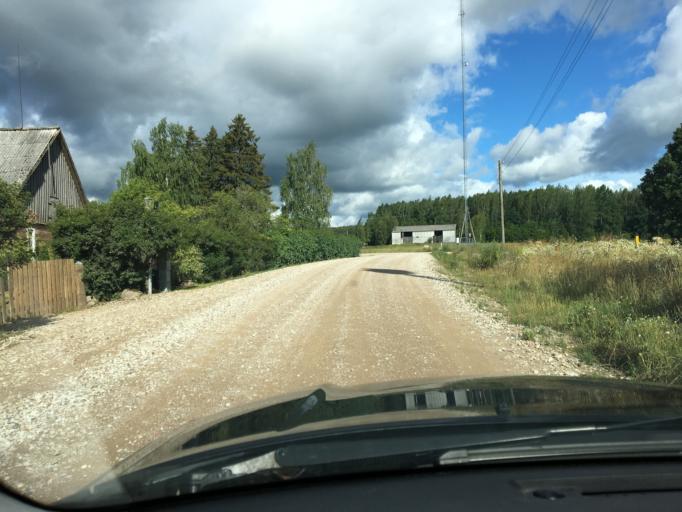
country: LV
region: Kuldigas Rajons
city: Kuldiga
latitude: 56.8426
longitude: 21.9354
